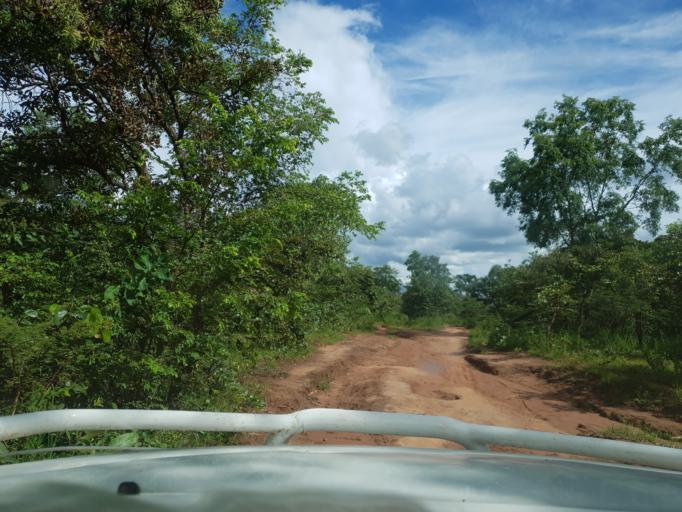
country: CI
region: Savanes
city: Tengrela
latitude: 10.4646
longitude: -6.7976
